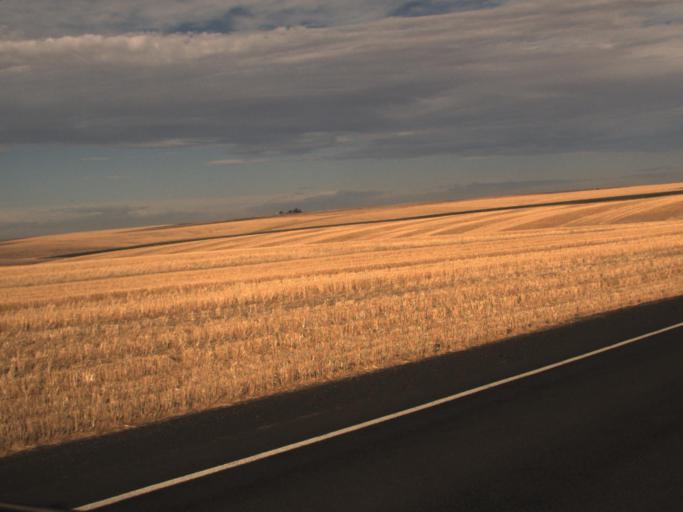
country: US
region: Washington
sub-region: Adams County
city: Ritzville
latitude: 47.1543
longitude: -118.6869
